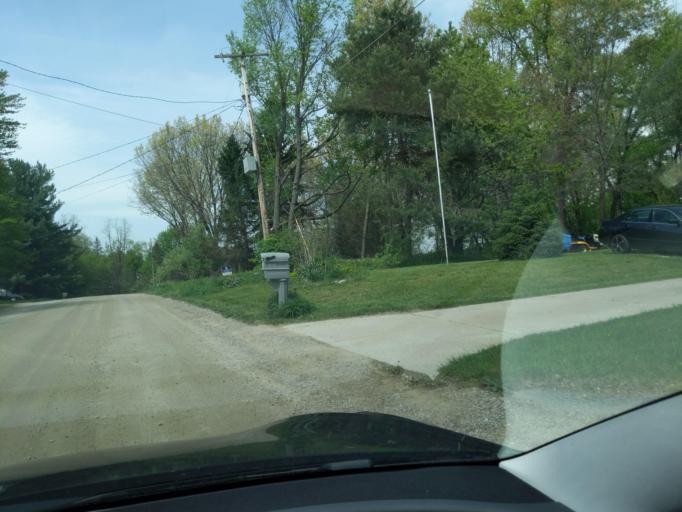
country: US
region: Michigan
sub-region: Ingham County
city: Stockbridge
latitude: 42.4269
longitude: -84.0739
